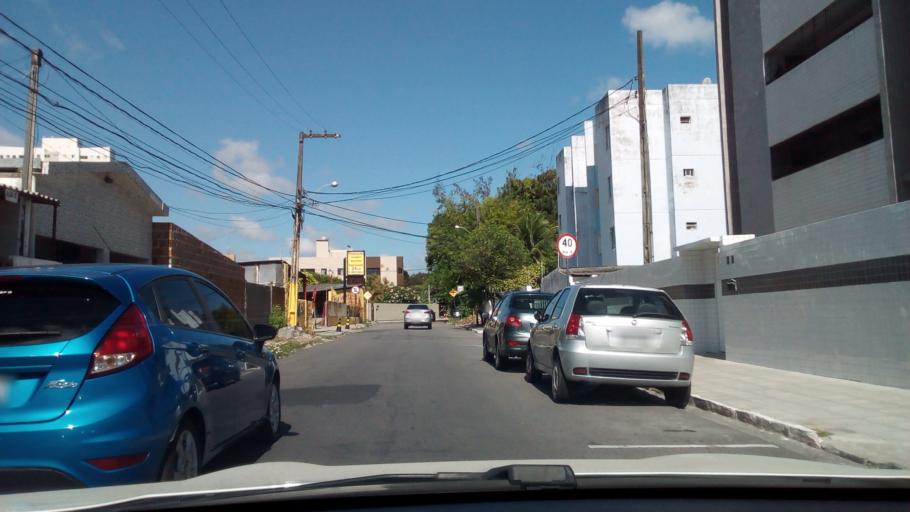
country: BR
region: Paraiba
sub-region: Joao Pessoa
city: Joao Pessoa
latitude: -7.1488
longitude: -34.8480
